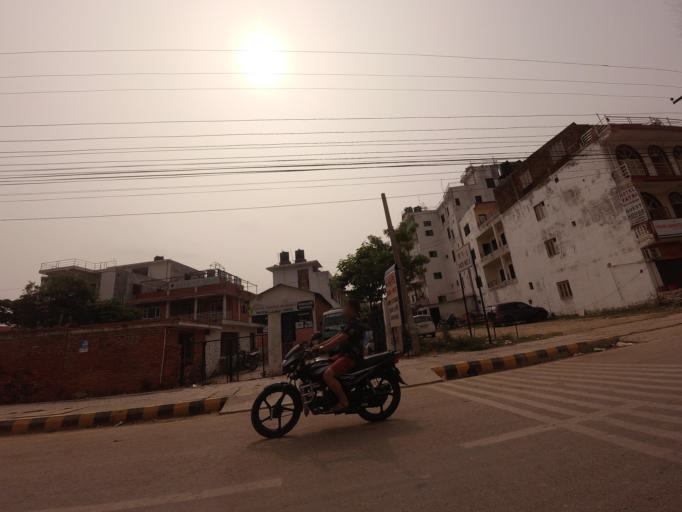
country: IN
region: Uttar Pradesh
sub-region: Maharajganj
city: Nautanwa
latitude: 27.4709
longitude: 83.2839
